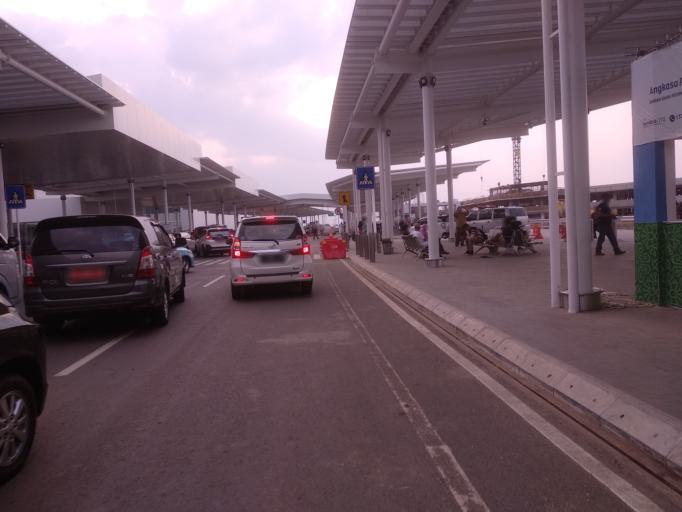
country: ID
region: Central Java
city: Semarang
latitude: -6.9662
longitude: 110.3758
